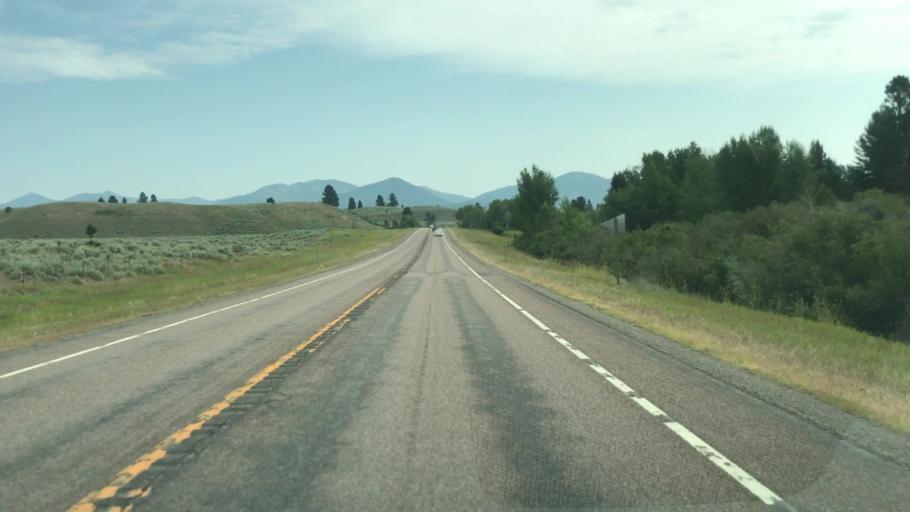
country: US
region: Montana
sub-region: Missoula County
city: Seeley Lake
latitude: 47.0367
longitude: -113.2286
